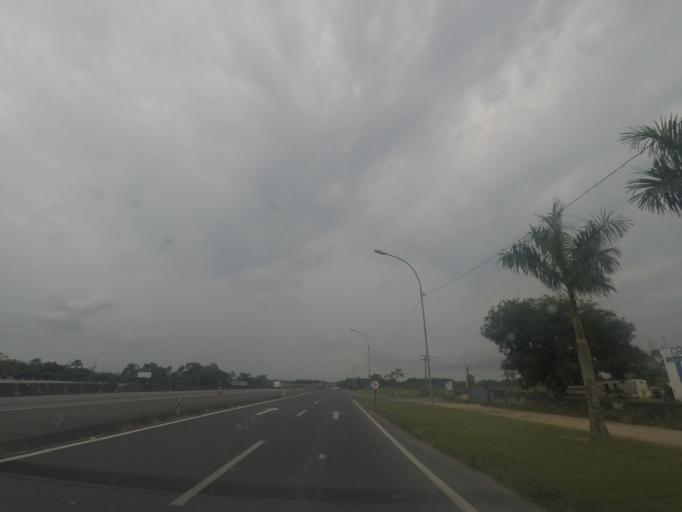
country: BR
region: Sao Paulo
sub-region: Registro
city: Registro
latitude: -24.5320
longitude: -47.8576
